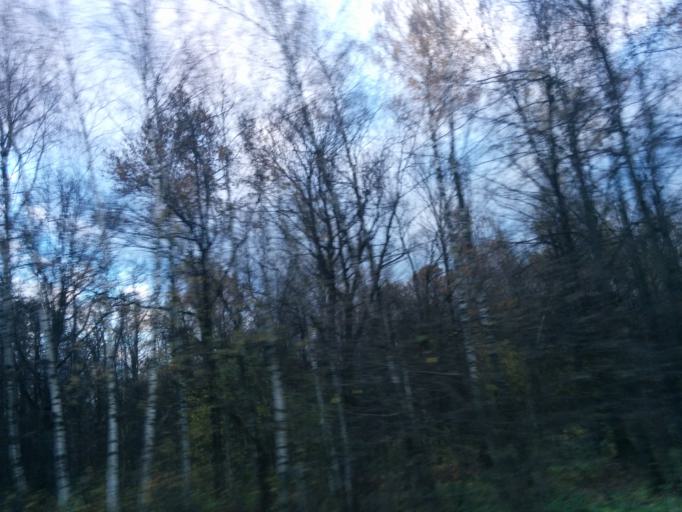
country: RU
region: Moscow
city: Annino
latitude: 55.5443
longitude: 37.6140
